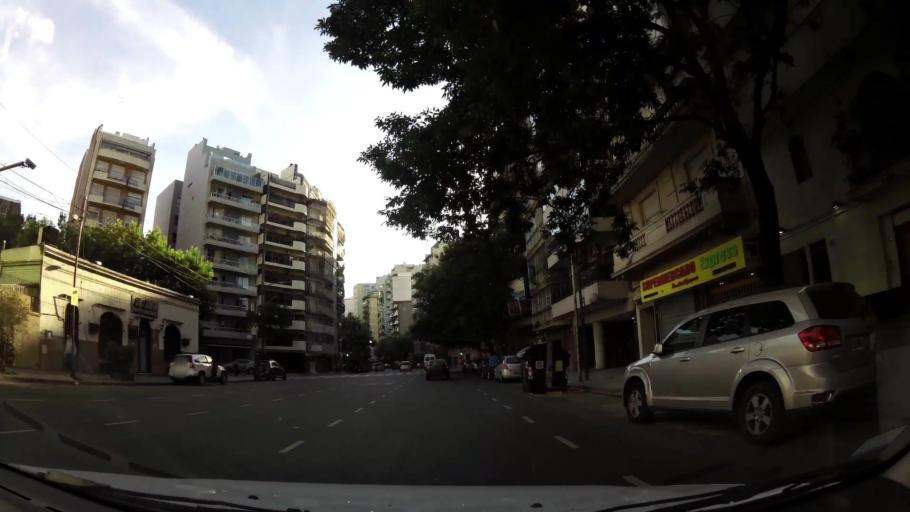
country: AR
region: Buenos Aires F.D.
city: Colegiales
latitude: -34.5988
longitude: -58.4285
